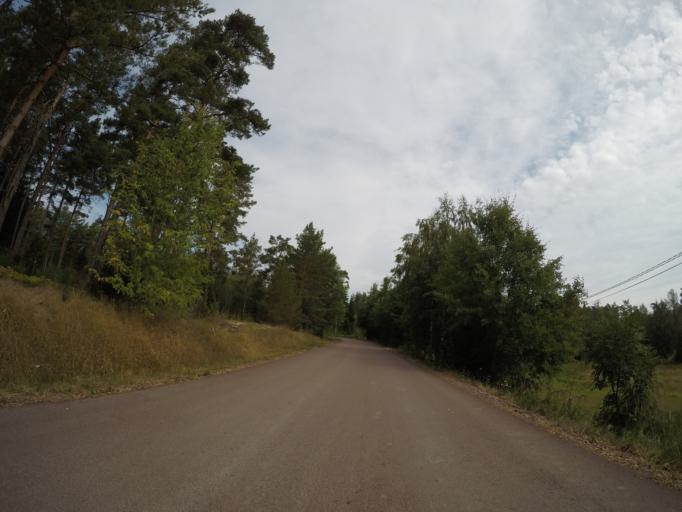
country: AX
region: Alands landsbygd
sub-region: Finstroem
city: Finstroem
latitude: 60.2539
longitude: 19.9145
